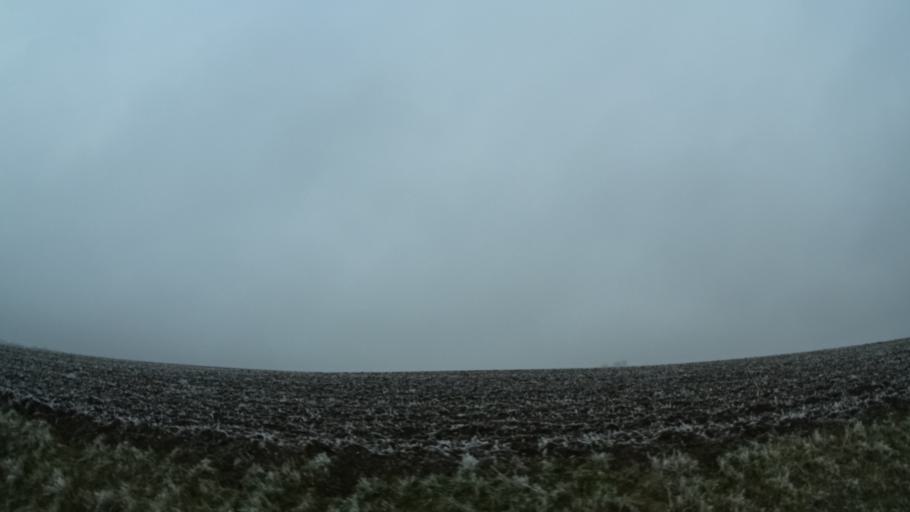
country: DE
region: Bavaria
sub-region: Regierungsbezirk Unterfranken
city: Butthard
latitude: 49.5588
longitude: 9.8393
